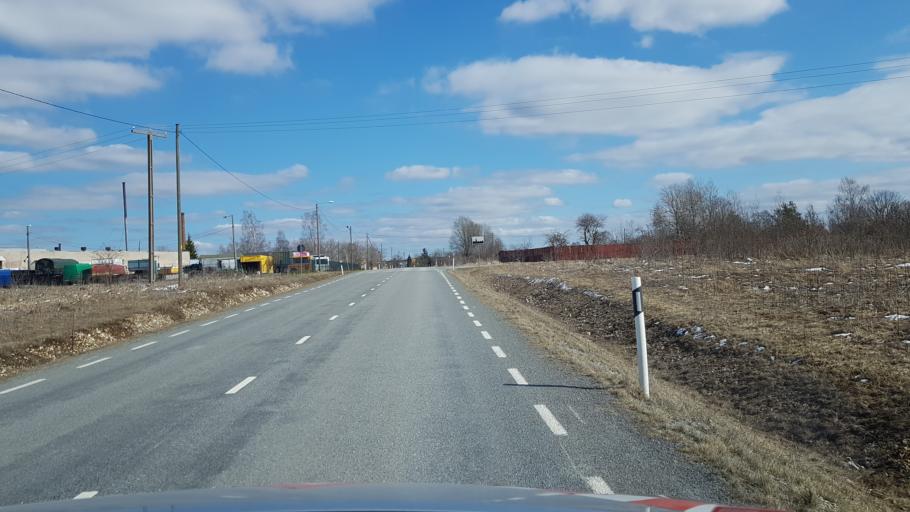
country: EE
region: Laeaene-Virumaa
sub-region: Tapa vald
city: Tapa
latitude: 59.2688
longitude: 25.9465
